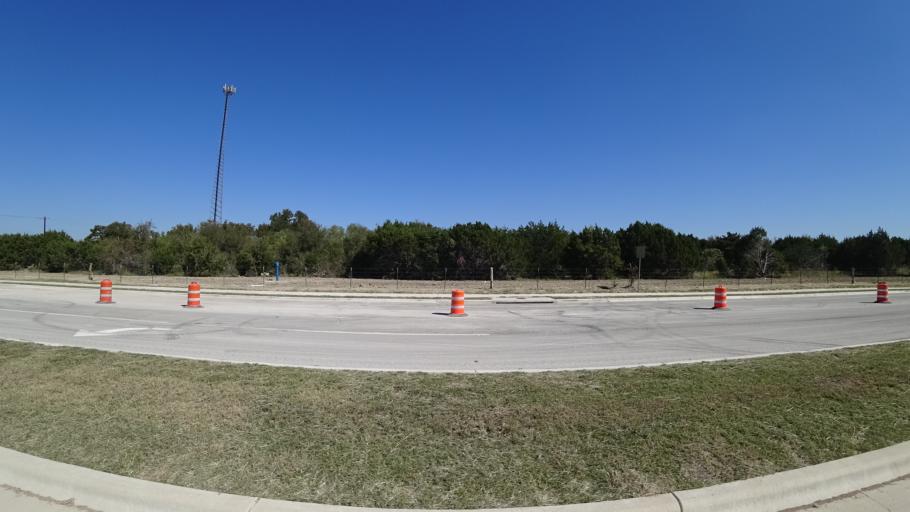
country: US
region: Texas
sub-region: Travis County
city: Hornsby Bend
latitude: 30.2753
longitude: -97.5989
